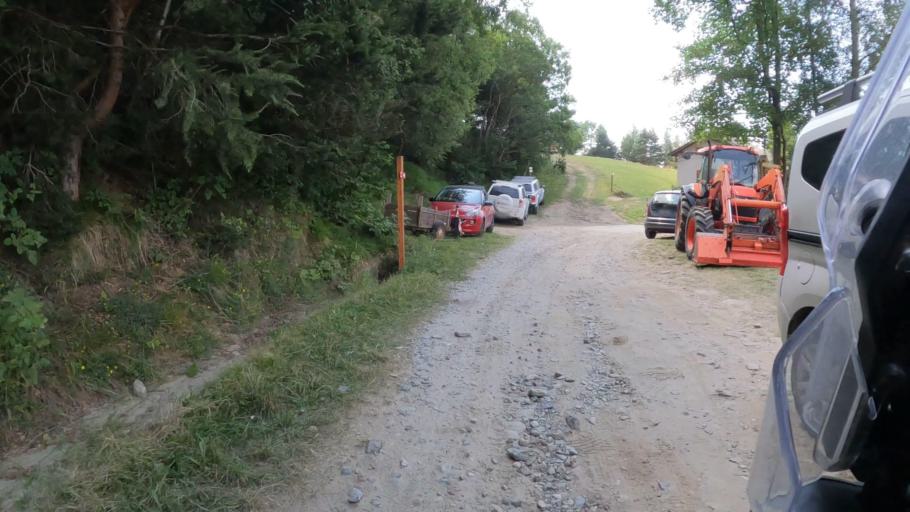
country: IT
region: Piedmont
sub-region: Provincia di Torino
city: Borgone Susa
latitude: 45.1574
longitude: 7.2630
